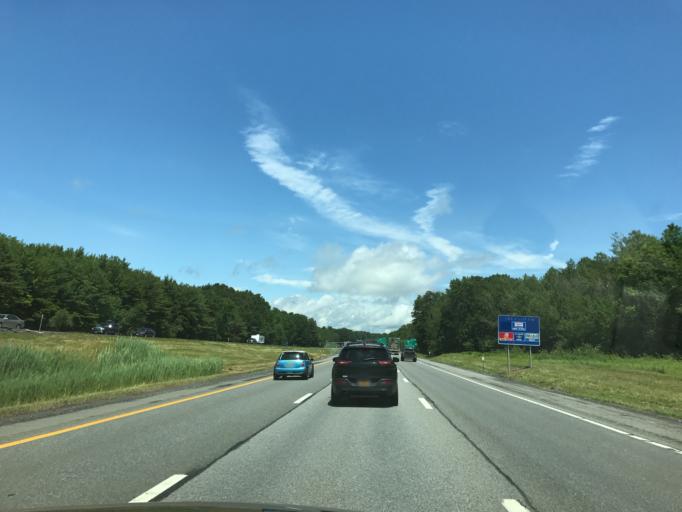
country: US
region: New York
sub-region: Warren County
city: West Glens Falls
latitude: 43.2281
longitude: -73.6918
